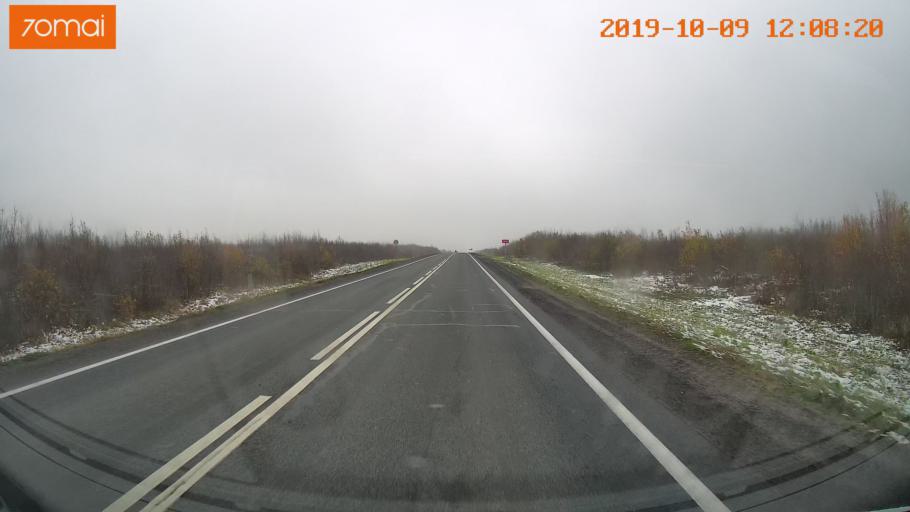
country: RU
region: Jaroslavl
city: Prechistoye
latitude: 58.5878
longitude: 40.3471
